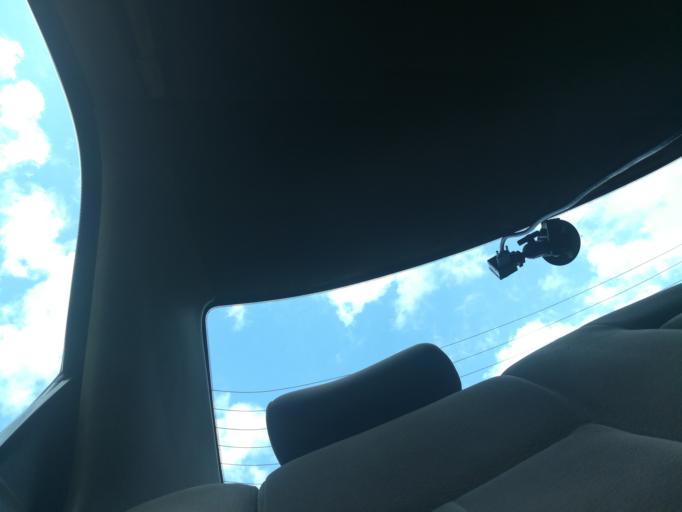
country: NG
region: Lagos
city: Ikorodu
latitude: 6.6634
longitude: 3.6186
